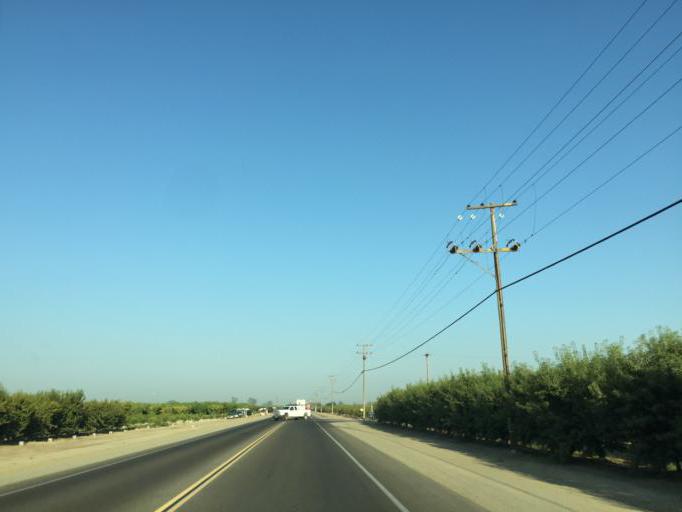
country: US
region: California
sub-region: Tulare County
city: London
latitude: 36.4887
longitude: -119.4928
